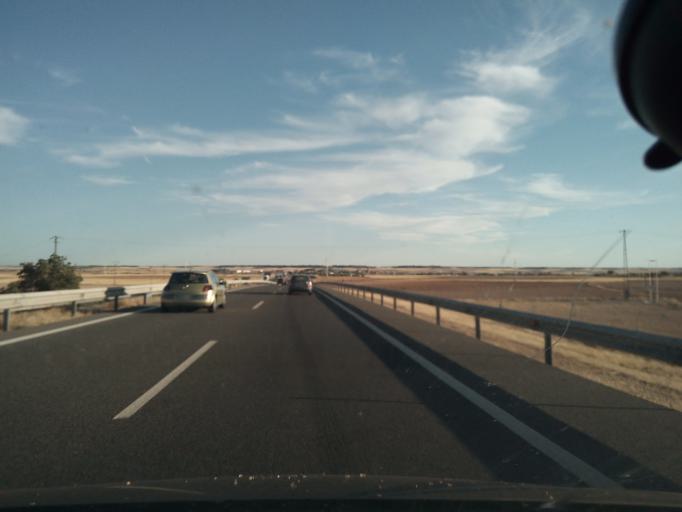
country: ES
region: Castille-La Mancha
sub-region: Province of Toledo
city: Tembleque
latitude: 39.7183
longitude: -3.4943
